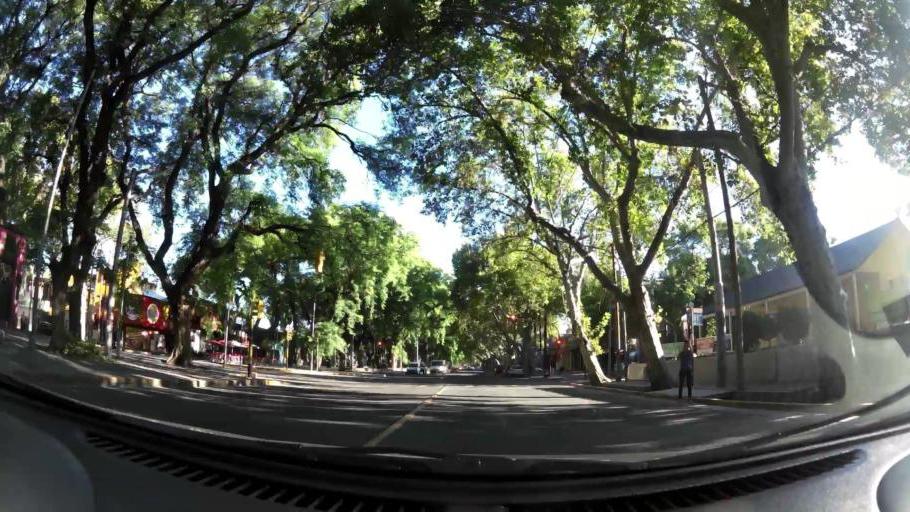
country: AR
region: Mendoza
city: Mendoza
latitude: -32.8760
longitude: -68.8356
